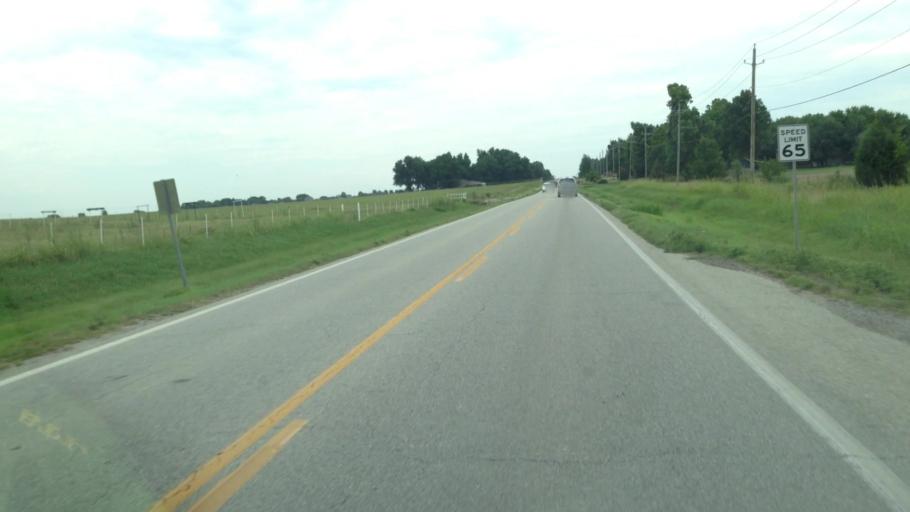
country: US
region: Oklahoma
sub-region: Craig County
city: Vinita
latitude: 36.6614
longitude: -95.1436
